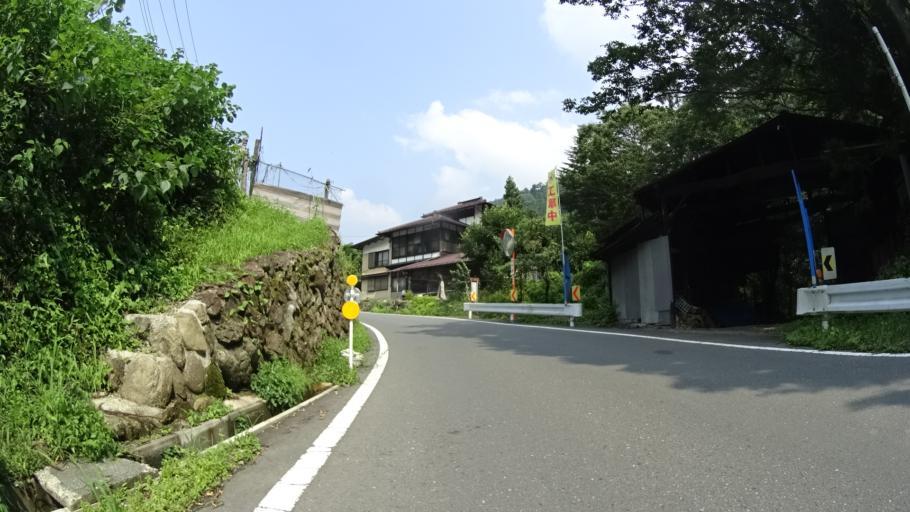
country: JP
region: Gunma
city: Tomioka
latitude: 36.0501
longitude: 138.8776
